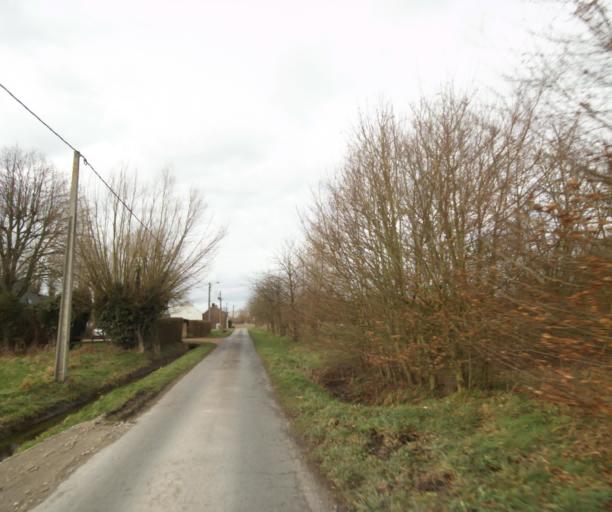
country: FR
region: Nord-Pas-de-Calais
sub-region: Departement du Nord
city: Hergnies
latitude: 50.4934
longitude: 3.5409
